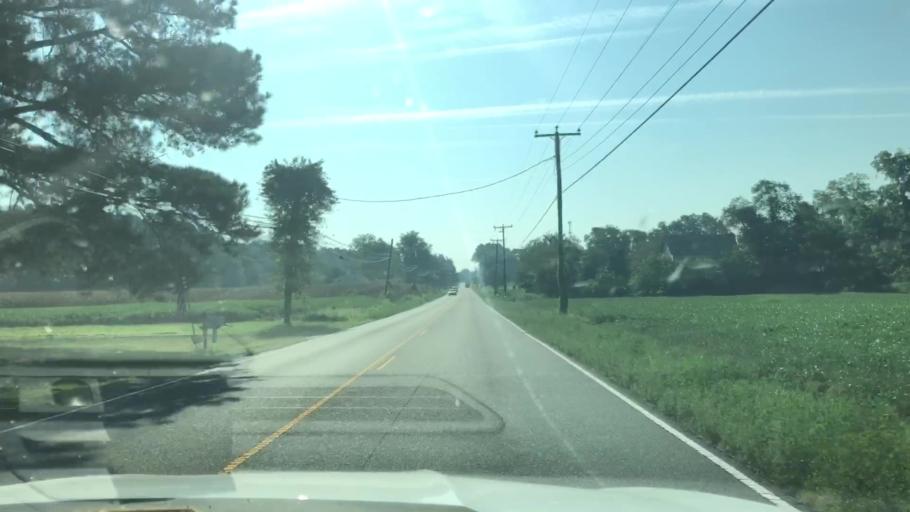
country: US
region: Virginia
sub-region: Richmond County
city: Warsaw
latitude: 37.8946
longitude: -76.6467
